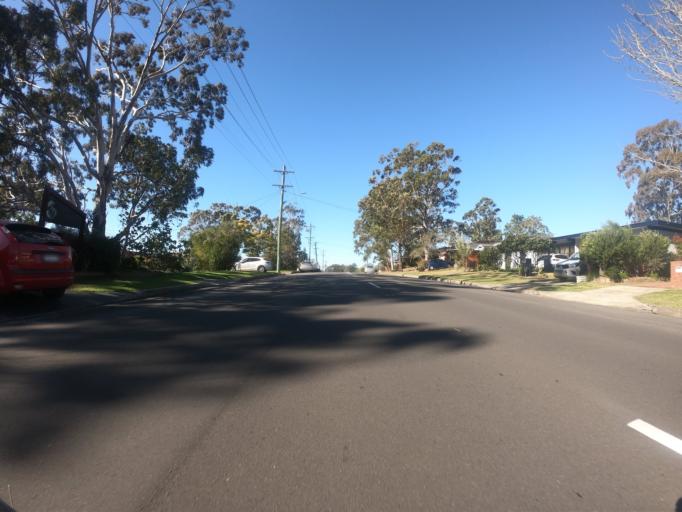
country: AU
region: New South Wales
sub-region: Wollongong
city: Mount Keira
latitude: -34.4257
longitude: 150.8517
